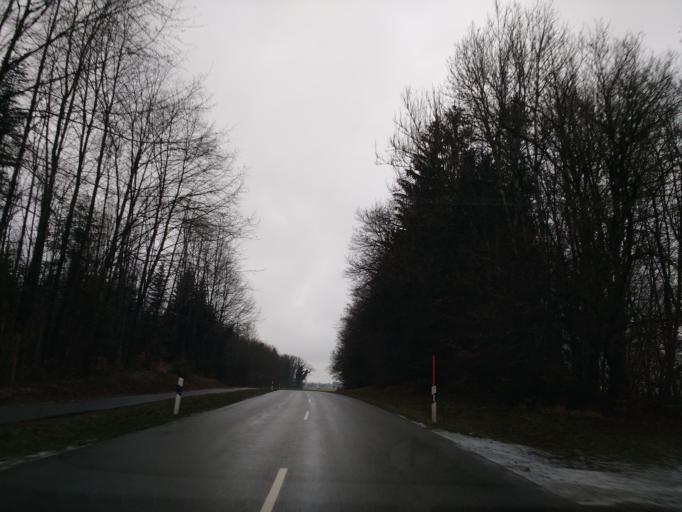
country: DE
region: Bavaria
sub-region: Swabia
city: Neuburg
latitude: 47.7702
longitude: 10.3673
